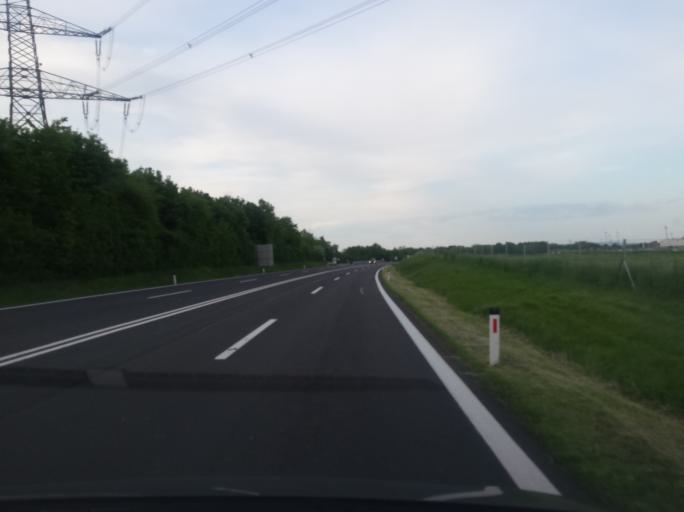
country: AT
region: Burgenland
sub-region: Politischer Bezirk Mattersburg
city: Mattersburg
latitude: 47.7382
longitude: 16.3730
